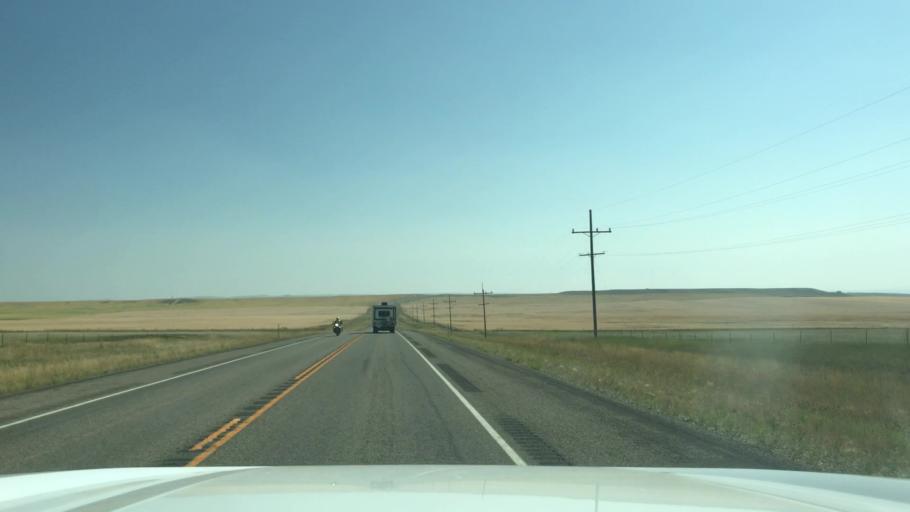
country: US
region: Montana
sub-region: Wheatland County
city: Harlowton
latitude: 46.4931
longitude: -109.7661
